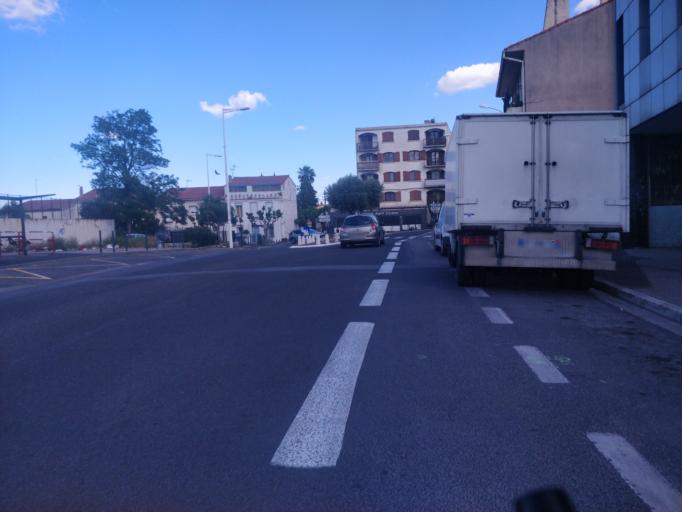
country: FR
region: Languedoc-Roussillon
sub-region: Departement des Pyrenees-Orientales
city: Perpignan
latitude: 42.6906
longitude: 2.9093
